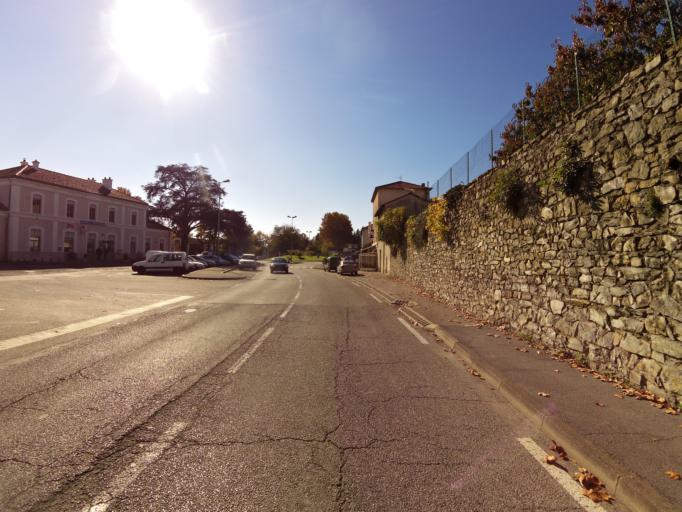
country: FR
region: Rhone-Alpes
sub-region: Departement de l'Ardeche
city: Aubenas
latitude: 44.6113
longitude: 4.3910
